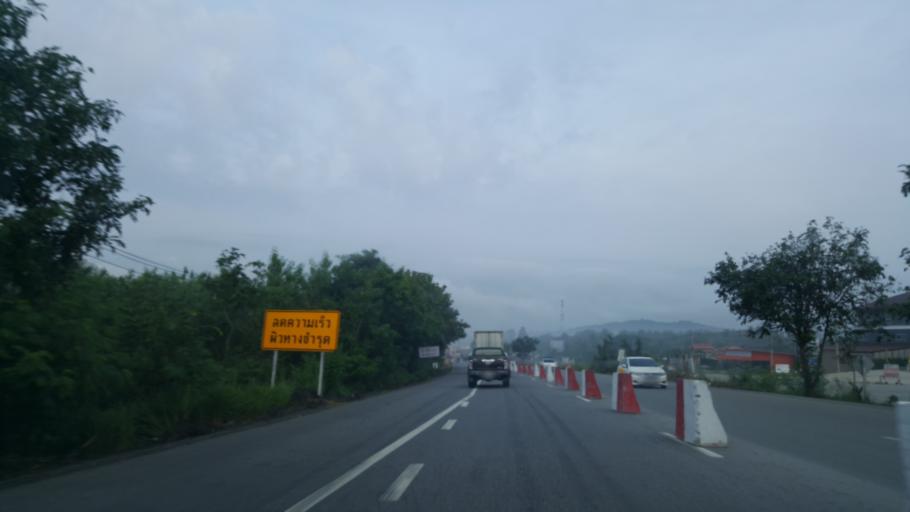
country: TH
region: Chon Buri
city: Phatthaya
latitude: 12.9161
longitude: 101.0216
